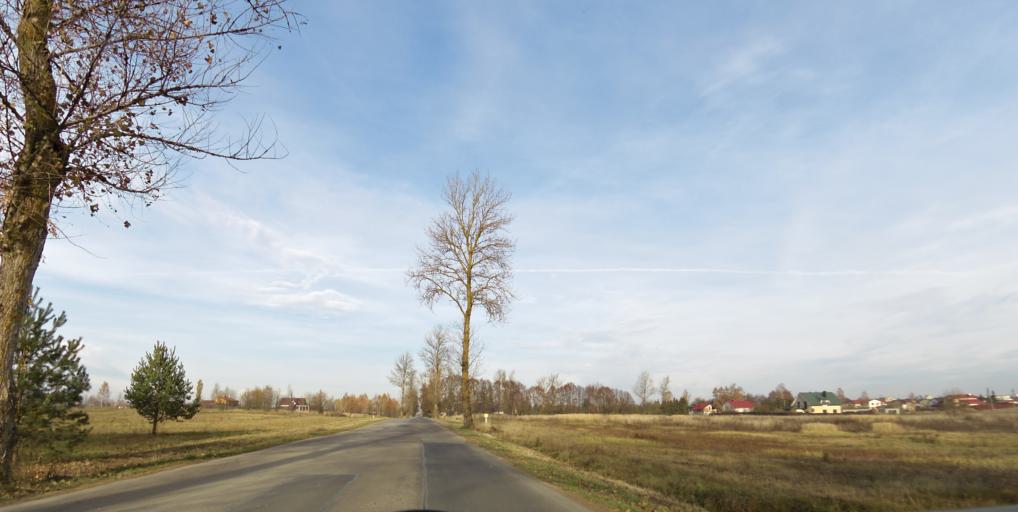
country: LT
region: Vilnius County
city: Pilaite
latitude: 54.7121
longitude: 25.1610
